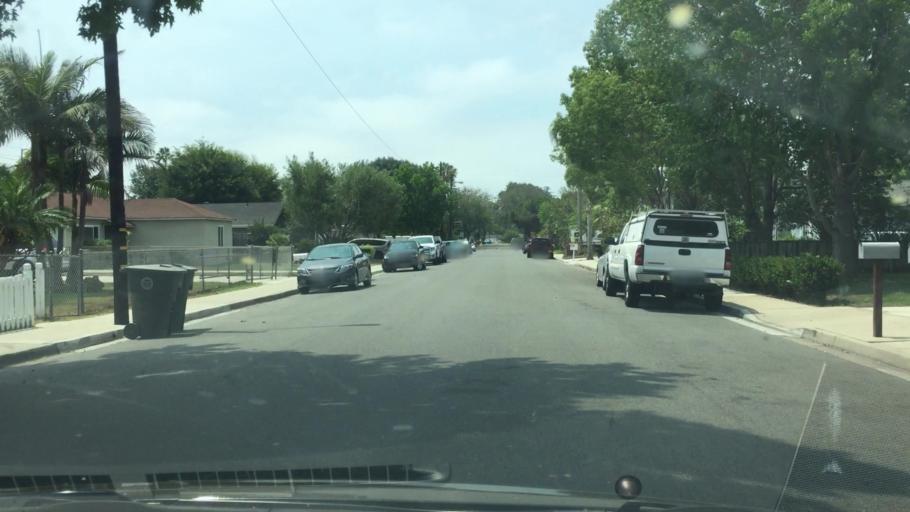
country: US
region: California
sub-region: Orange County
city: Costa Mesa
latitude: 33.6519
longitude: -117.9370
